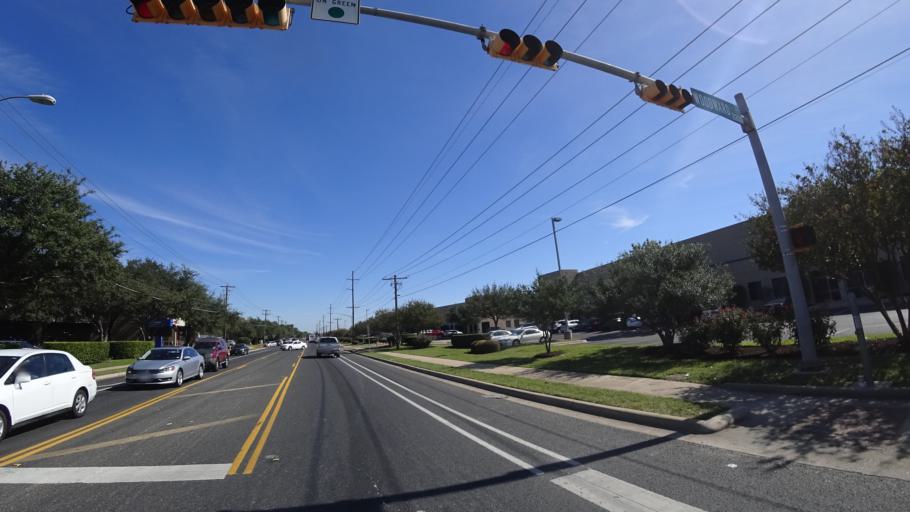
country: US
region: Texas
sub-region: Travis County
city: Austin
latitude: 30.2102
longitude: -97.7473
